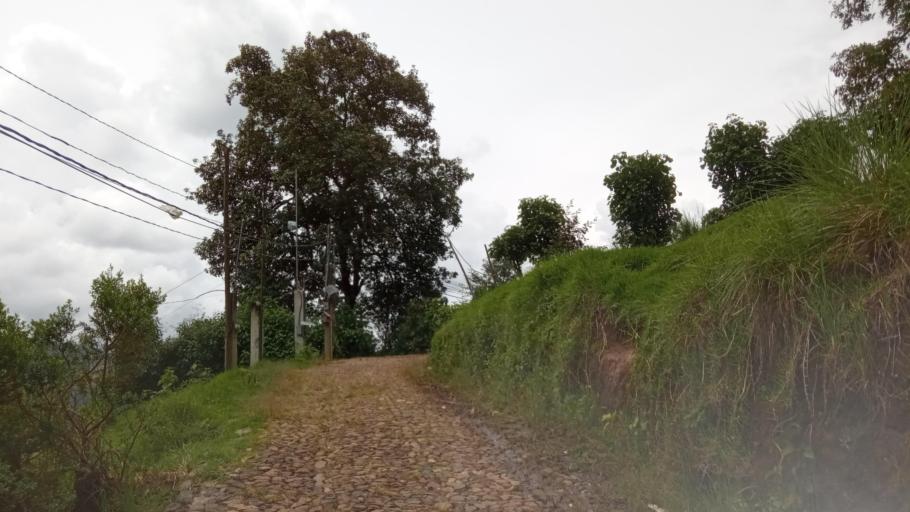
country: GT
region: San Marcos
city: Tejutla
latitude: 15.1165
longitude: -91.8058
